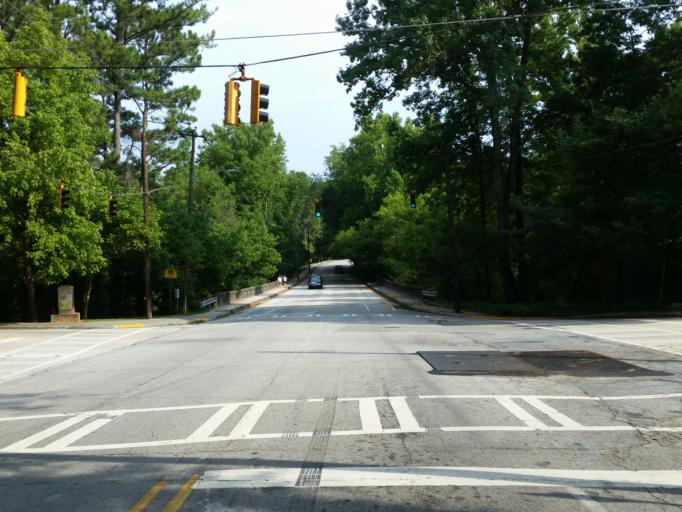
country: US
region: Georgia
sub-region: Cobb County
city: Vinings
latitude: 33.8252
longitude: -84.4168
